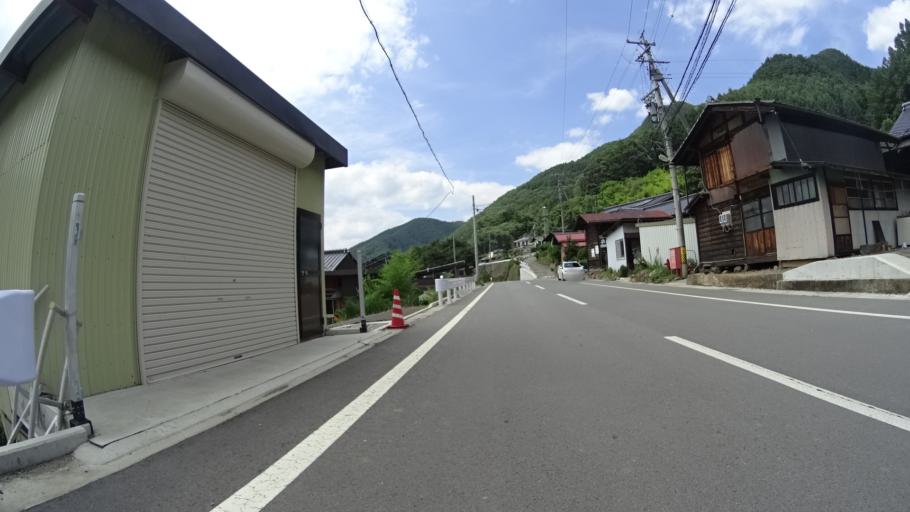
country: JP
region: Nagano
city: Saku
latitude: 36.0585
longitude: 138.5614
